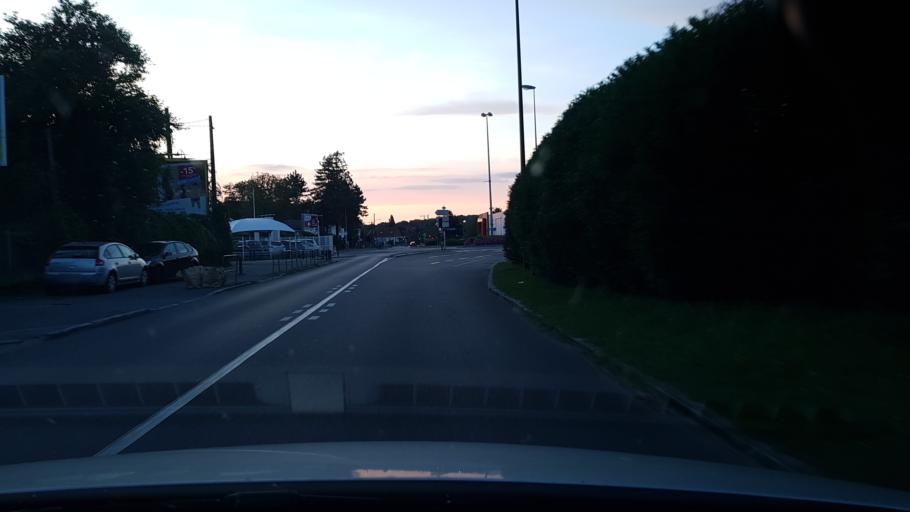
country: FR
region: Ile-de-France
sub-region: Departement de l'Essonne
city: Orsay
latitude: 48.6836
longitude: 2.1888
